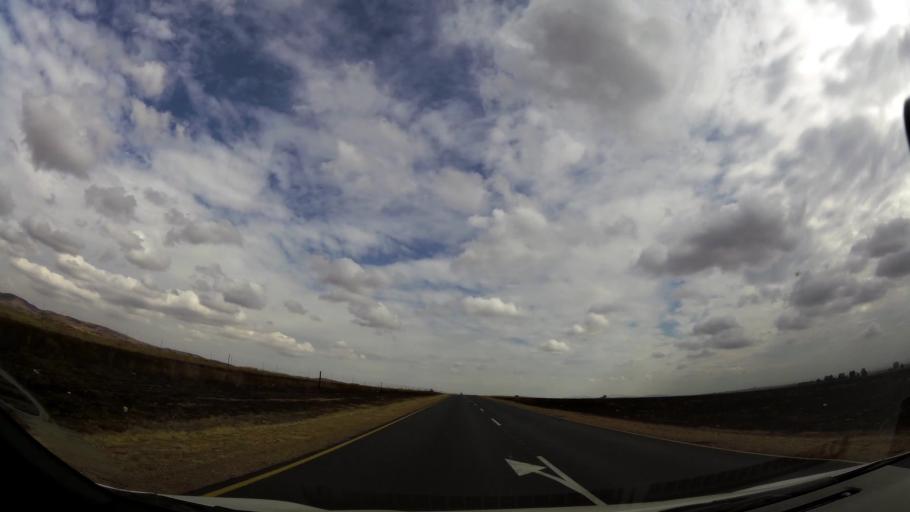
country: ZA
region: Gauteng
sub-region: Sedibeng District Municipality
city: Heidelberg
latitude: -26.4378
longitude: 28.2325
